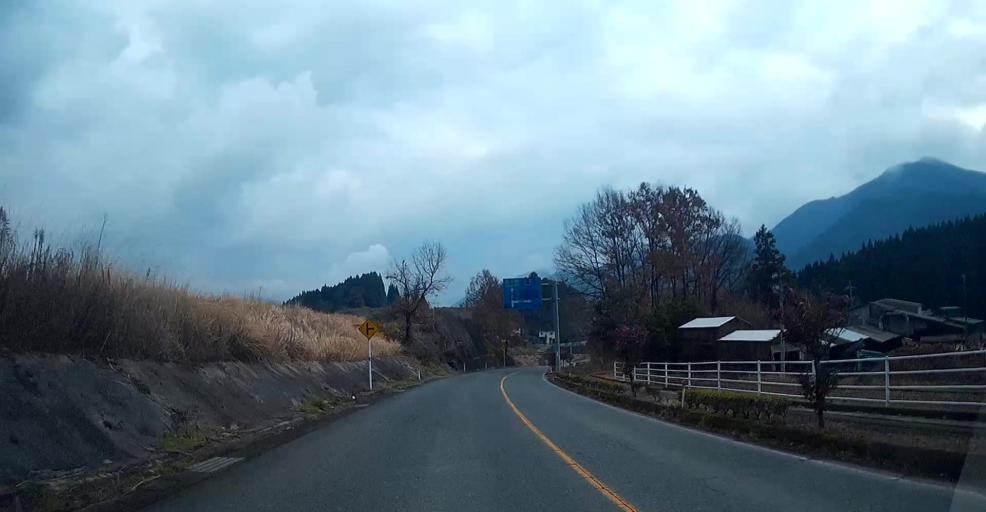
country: JP
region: Kumamoto
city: Matsubase
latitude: 32.6242
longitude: 130.8771
